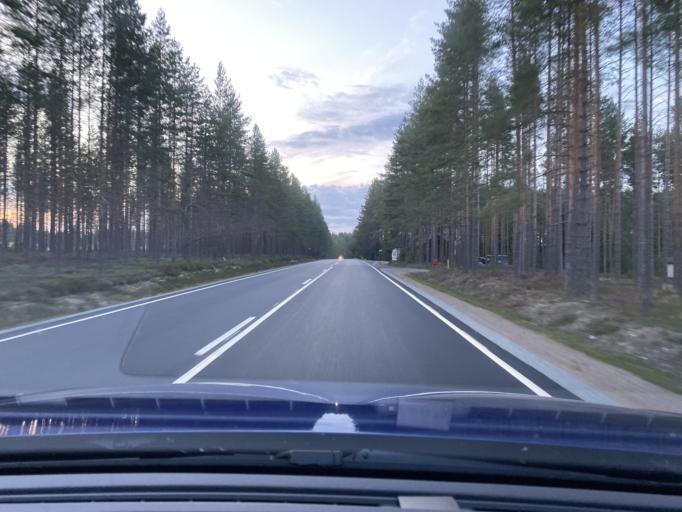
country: FI
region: Satakunta
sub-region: Pohjois-Satakunta
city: Honkajoki
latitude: 62.0618
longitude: 22.2492
